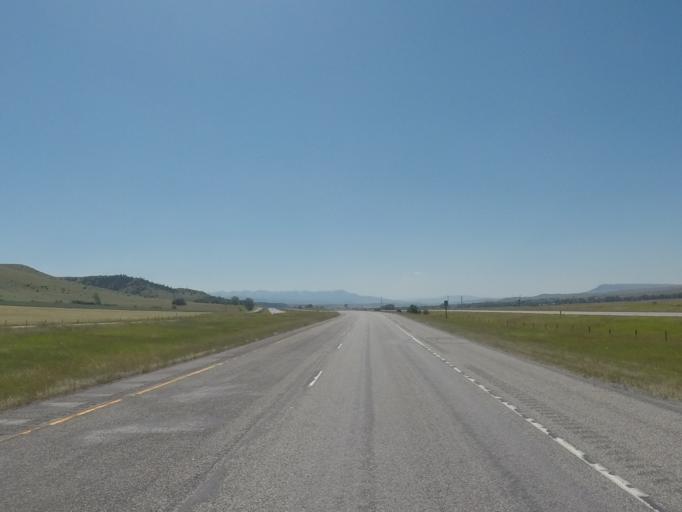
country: US
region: Montana
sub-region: Sweet Grass County
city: Big Timber
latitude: 45.8073
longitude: -110.0168
